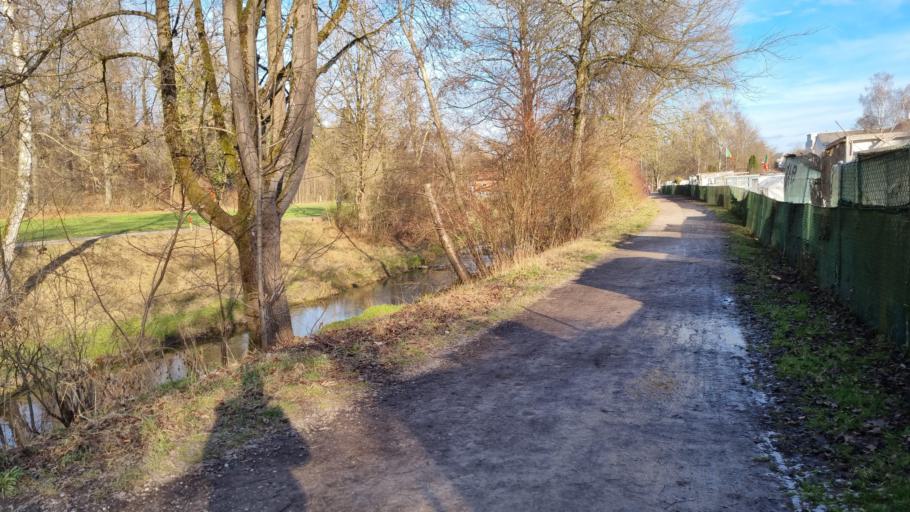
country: CH
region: Zurich
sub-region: Bezirk Uster
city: Duebendorf / Kunklerstrasse
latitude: 47.4061
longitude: 8.6202
